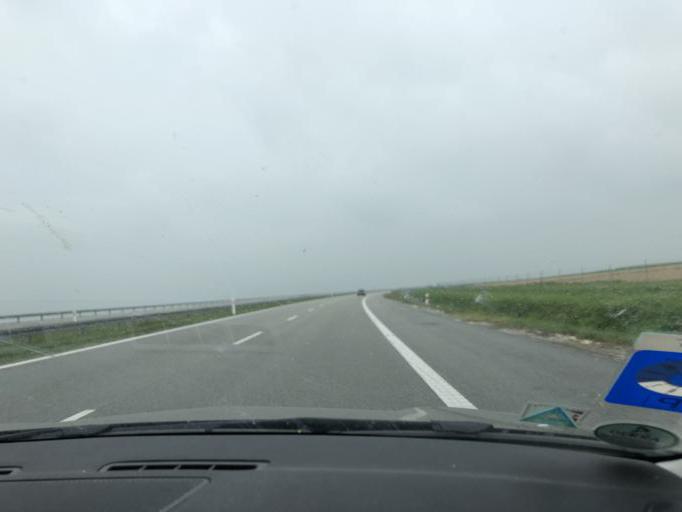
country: PL
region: Subcarpathian Voivodeship
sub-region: Powiat debicki
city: Czarna
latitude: 50.0880
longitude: 21.3183
